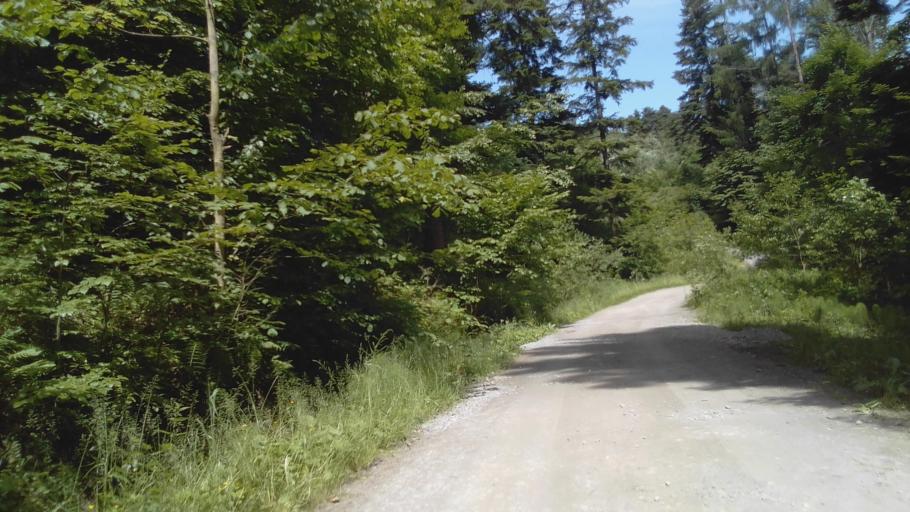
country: PL
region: Subcarpathian Voivodeship
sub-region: Powiat strzyzowski
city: Strzyzow
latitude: 49.8563
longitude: 21.8309
